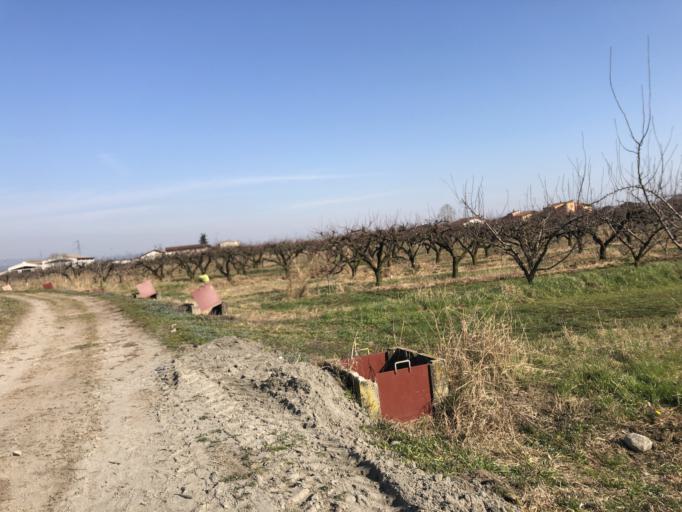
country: IT
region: Veneto
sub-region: Provincia di Verona
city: Lugagnano
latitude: 45.4190
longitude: 10.8774
